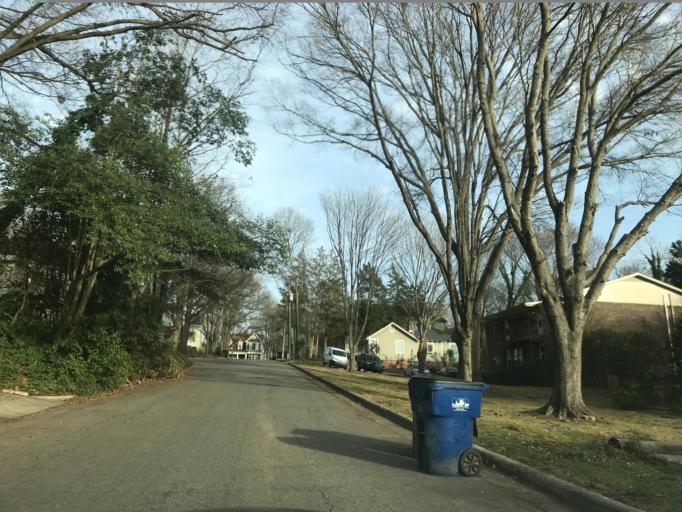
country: US
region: North Carolina
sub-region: Wake County
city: West Raleigh
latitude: 35.7927
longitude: -78.6669
